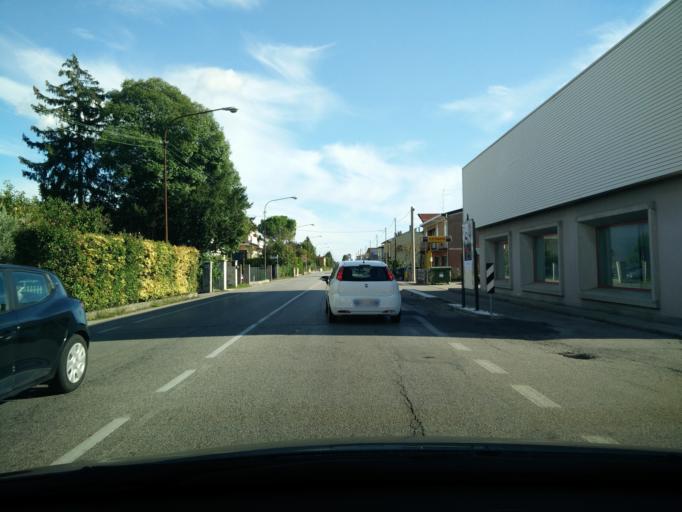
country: IT
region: Veneto
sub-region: Provincia di Venezia
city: Noventa di Piave
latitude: 45.6579
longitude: 12.5333
